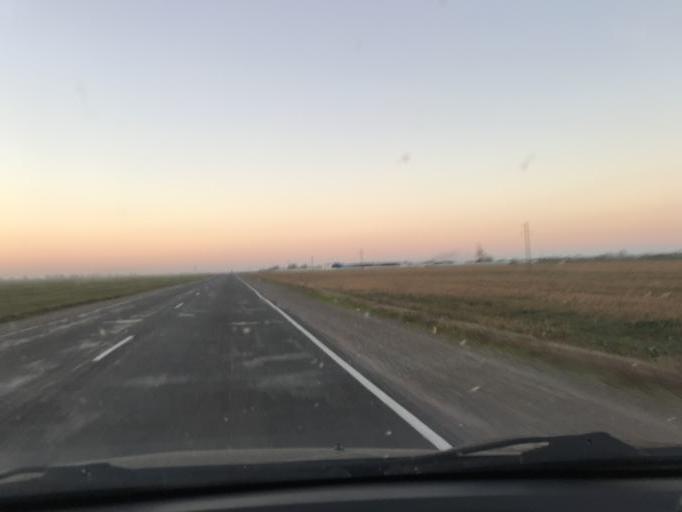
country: BY
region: Gomel
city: Horad Rechytsa
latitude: 52.2413
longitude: 30.5027
